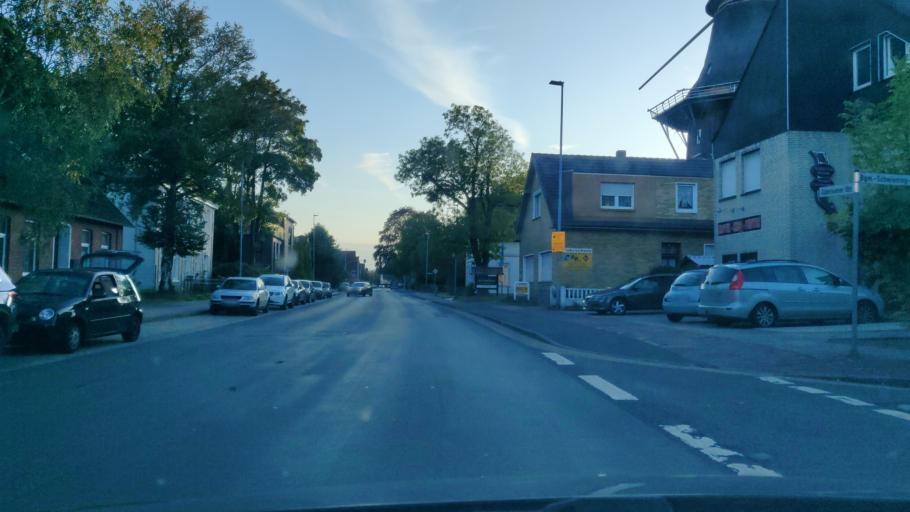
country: DE
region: Lower Saxony
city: Aurich
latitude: 53.4681
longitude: 7.4725
